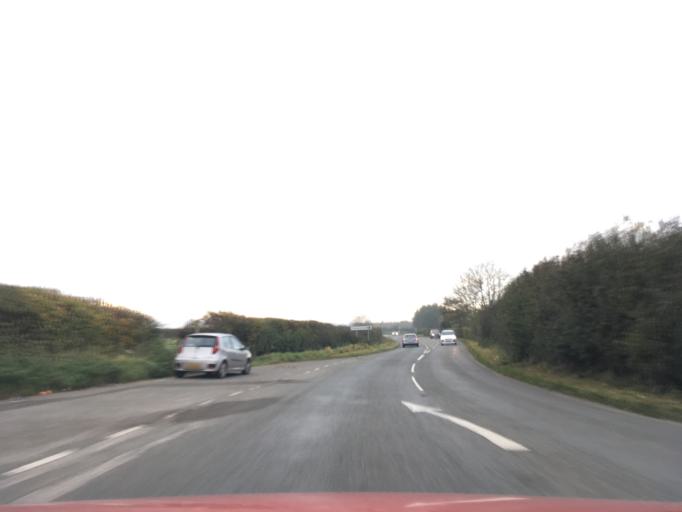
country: GB
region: England
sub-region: South Gloucestershire
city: Pucklechurch
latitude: 51.5062
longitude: -2.4273
